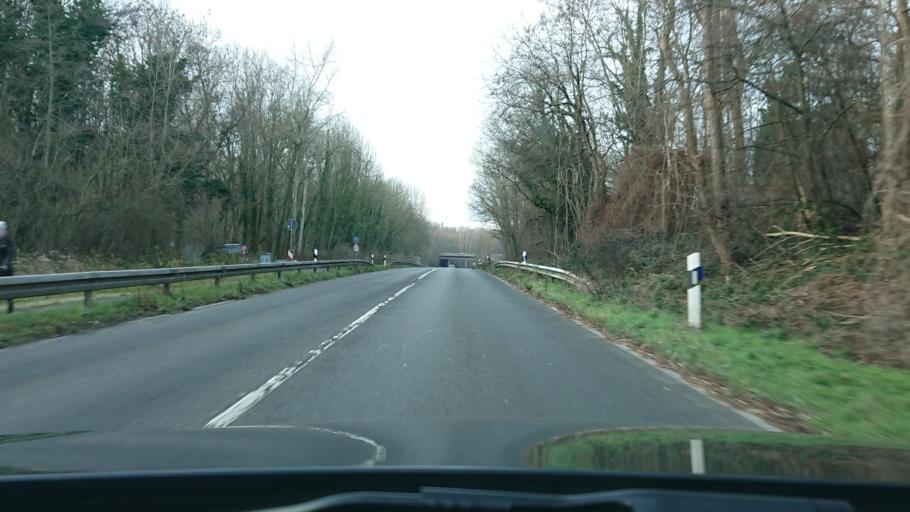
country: DE
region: North Rhine-Westphalia
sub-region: Regierungsbezirk Koln
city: Frechen
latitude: 50.8870
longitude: 6.8202
